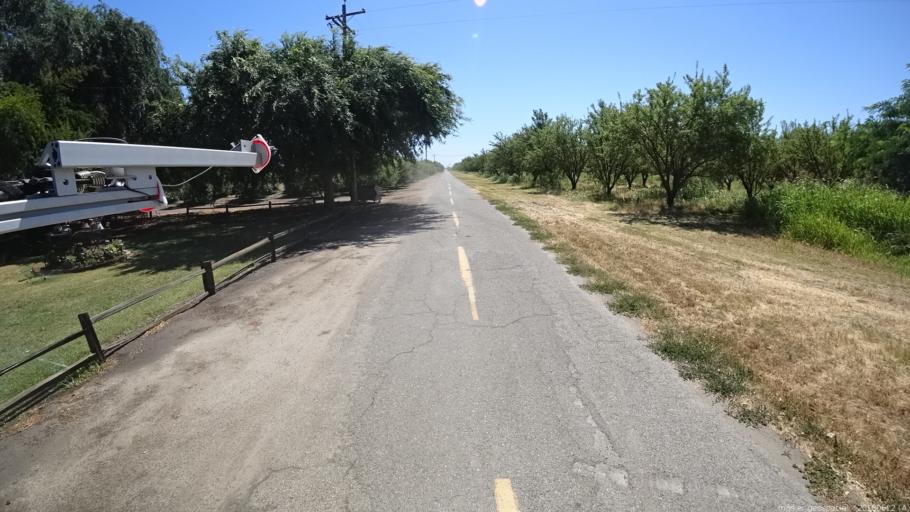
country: US
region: California
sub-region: Madera County
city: Chowchilla
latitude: 37.0255
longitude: -120.3039
